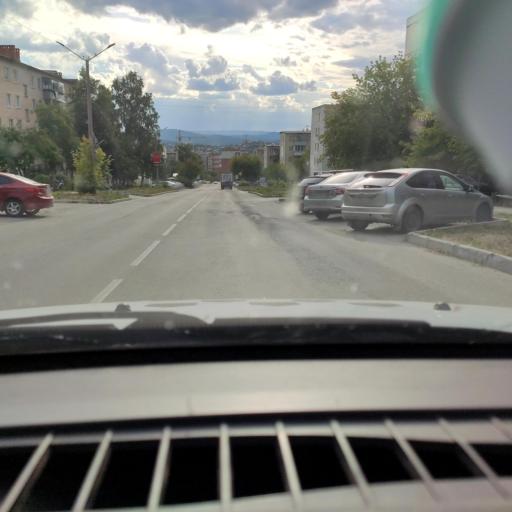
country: RU
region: Chelyabinsk
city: Miass
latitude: 55.0634
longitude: 60.1212
